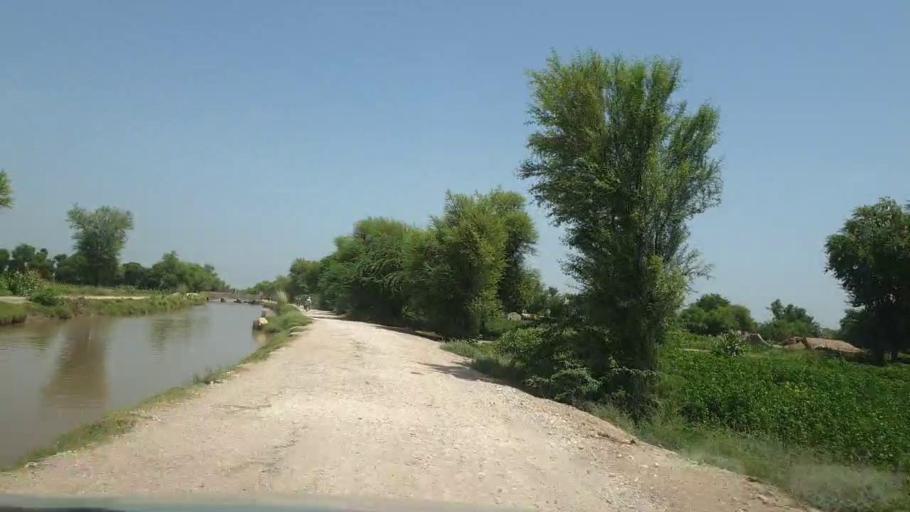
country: PK
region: Sindh
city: Pano Aqil
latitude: 27.6487
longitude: 69.1058
